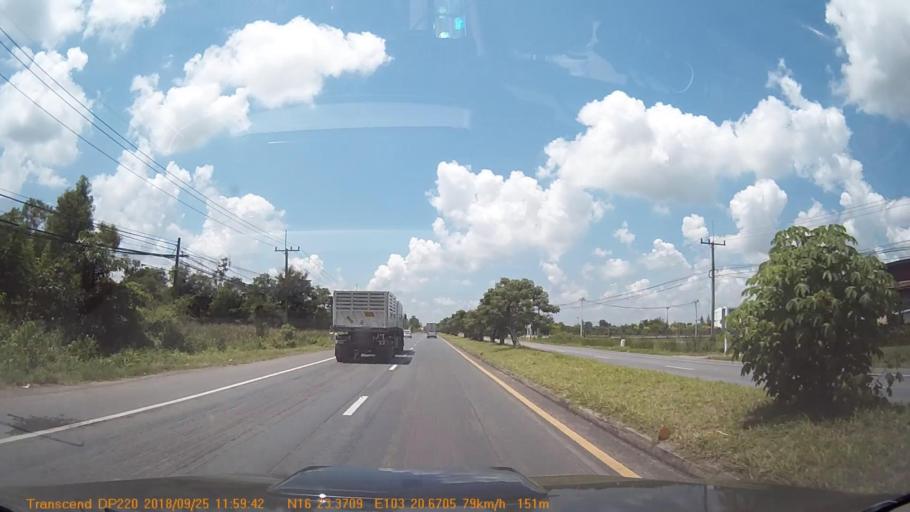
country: TH
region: Kalasin
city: Yang Talat
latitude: 16.3895
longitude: 103.3443
